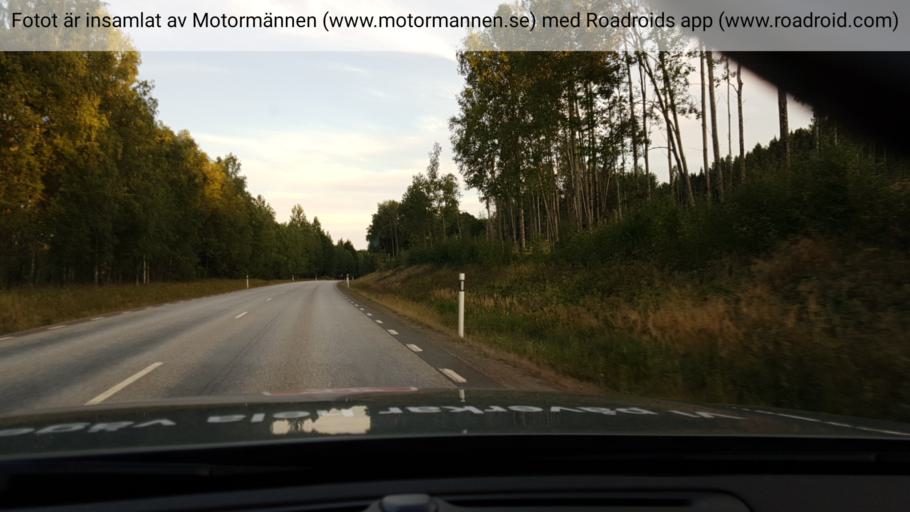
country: SE
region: Vaermland
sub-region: Storfors Kommun
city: Storfors
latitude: 59.5237
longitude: 14.3002
